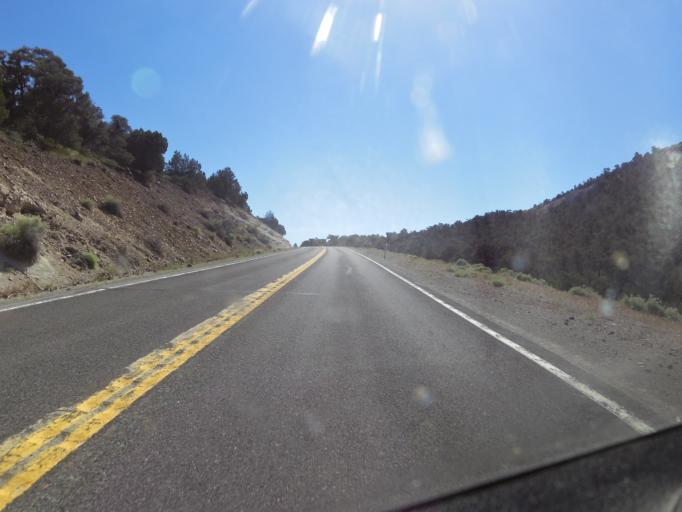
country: US
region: Nevada
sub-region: White Pine County
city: Ely
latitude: 38.8180
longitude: -115.2869
